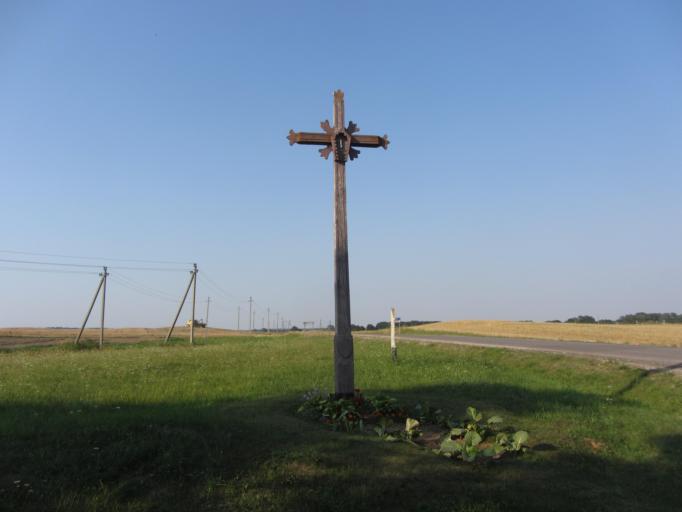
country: LT
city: Lazdijai
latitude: 54.1308
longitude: 23.5208
